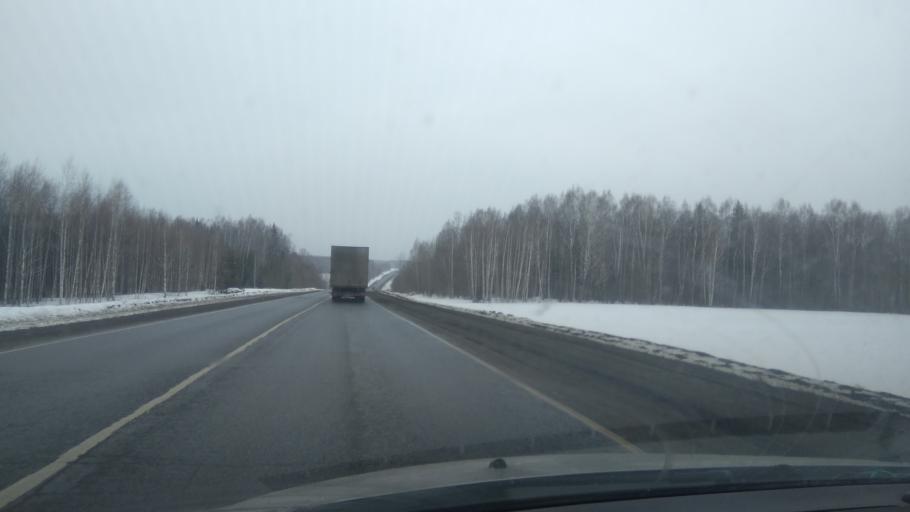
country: RU
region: Perm
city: Ust'-Kishert'
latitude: 57.1743
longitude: 57.1398
